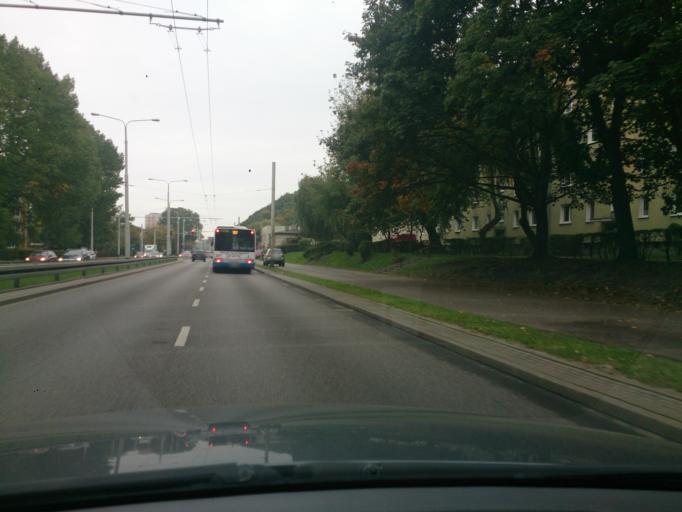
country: PL
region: Pomeranian Voivodeship
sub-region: Gdynia
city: Pogorze
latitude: 54.5393
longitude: 18.4689
